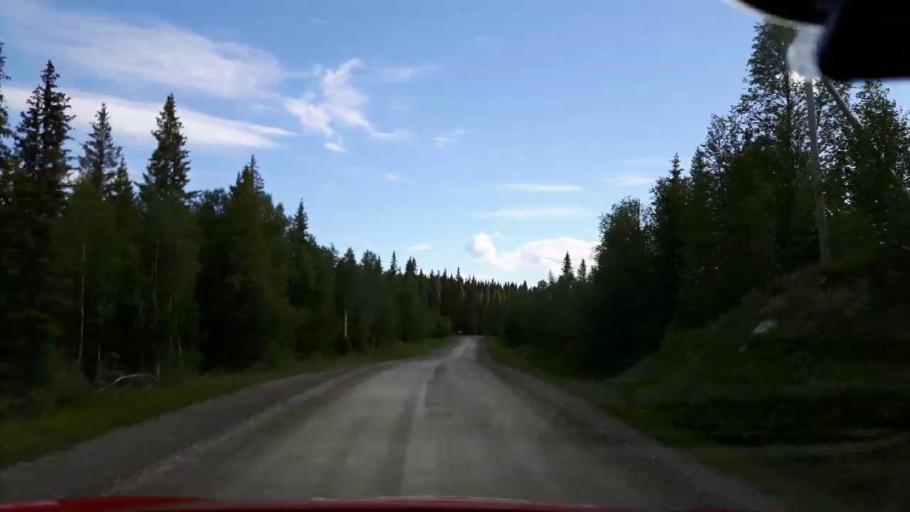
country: SE
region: Jaemtland
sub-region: Krokoms Kommun
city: Valla
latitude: 63.7861
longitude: 14.0485
